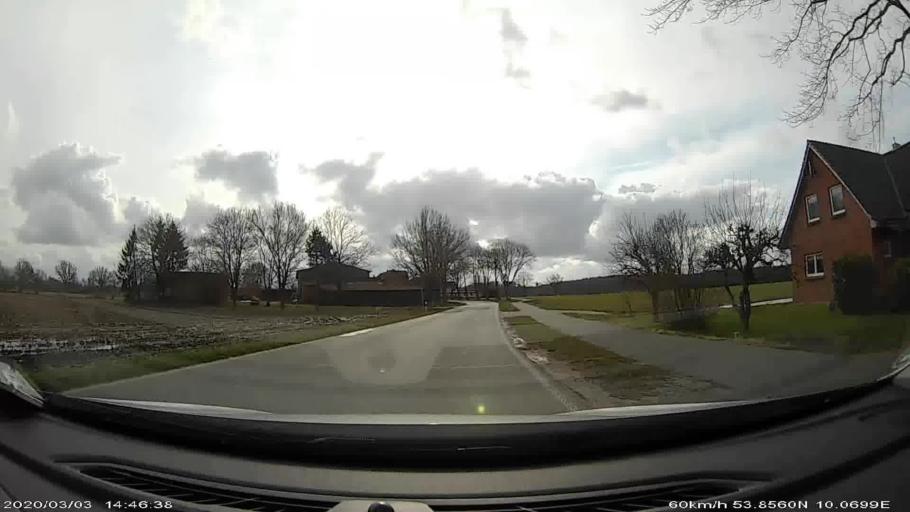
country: DE
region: Schleswig-Holstein
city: Huttblek
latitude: 53.8553
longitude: 10.0691
